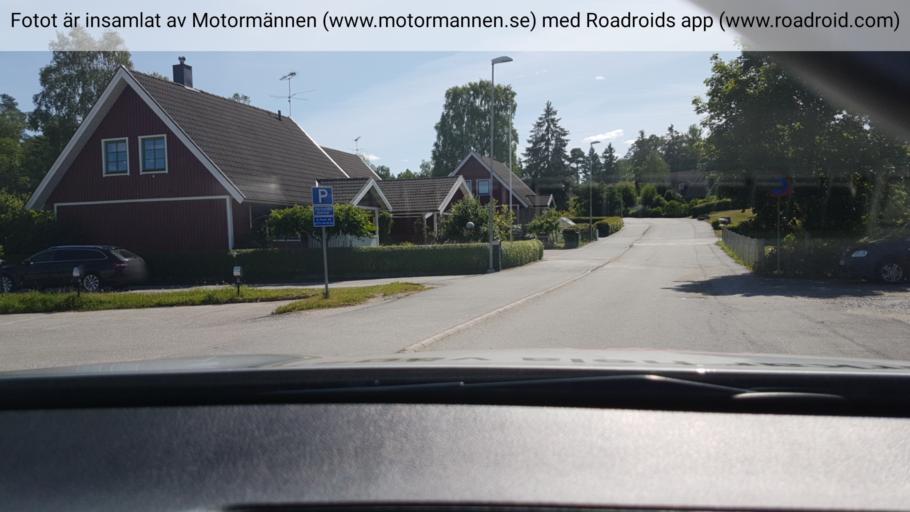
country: SE
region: Stockholm
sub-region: Sigtuna Kommun
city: Rosersberg
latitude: 59.5825
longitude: 17.8873
